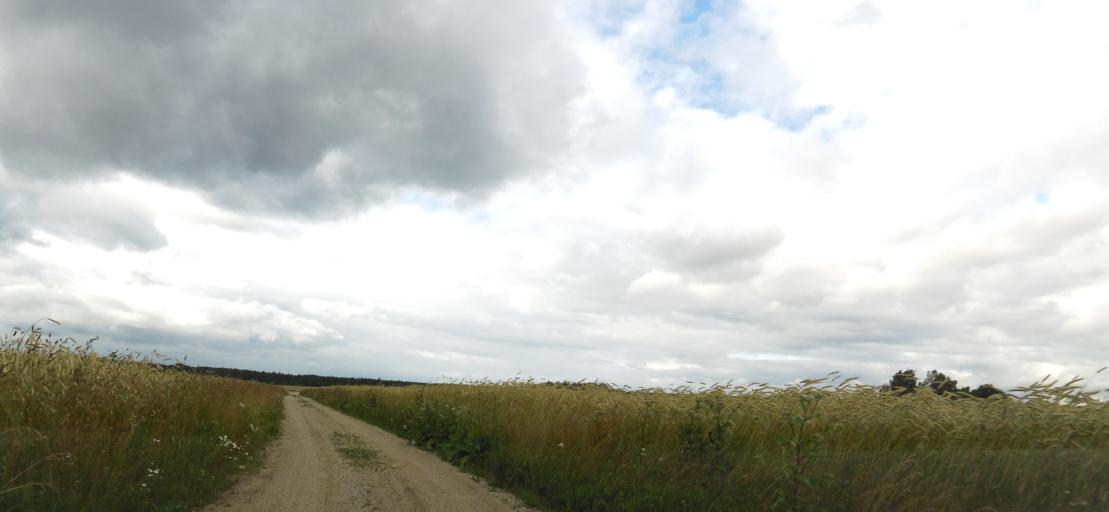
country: LT
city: Obeliai
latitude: 56.0716
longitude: 25.1045
